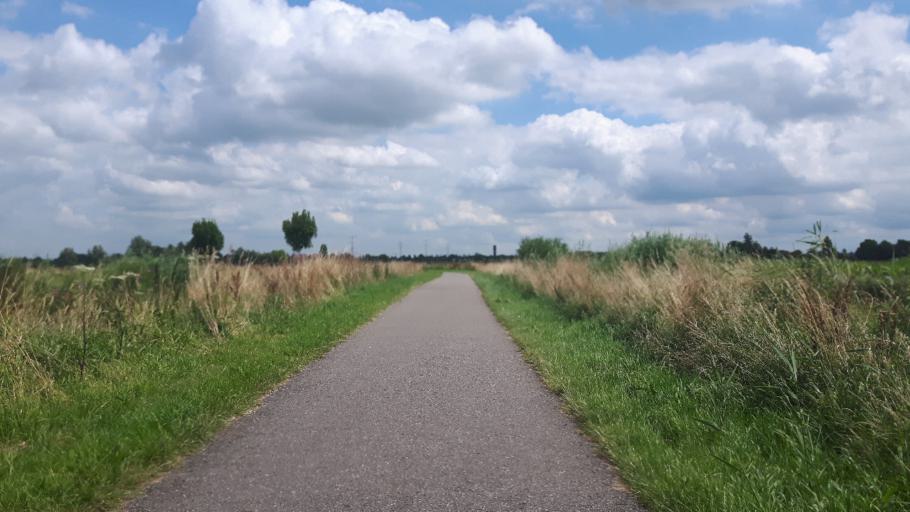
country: NL
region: South Holland
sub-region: Gemeente Krimpen aan den IJssel
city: Krimpen aan den IJssel
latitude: 51.9044
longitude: 4.6150
